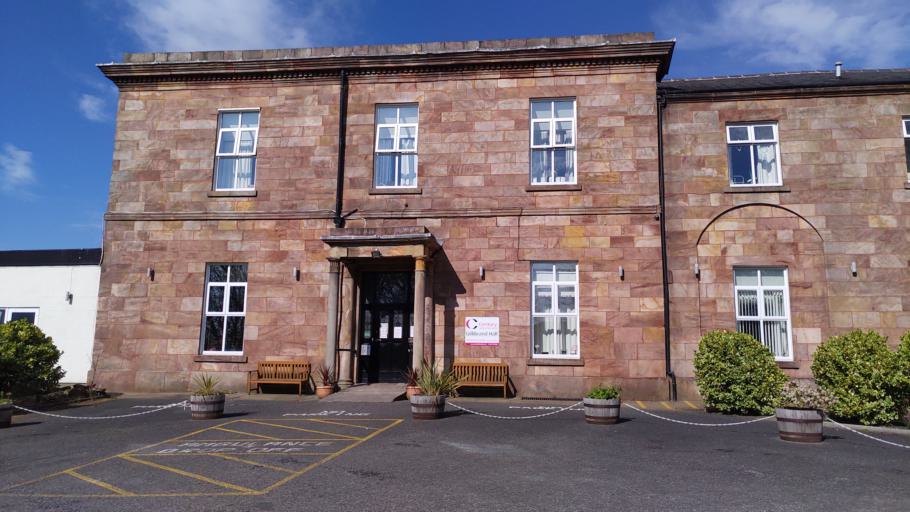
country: GB
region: England
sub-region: Lancashire
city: Coppull
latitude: 53.6454
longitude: -2.6467
